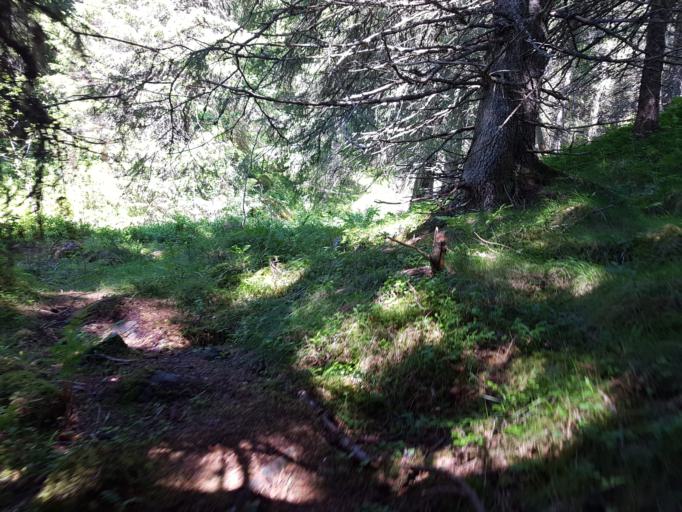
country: NO
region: Sor-Trondelag
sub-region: Melhus
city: Melhus
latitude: 63.4323
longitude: 10.2405
